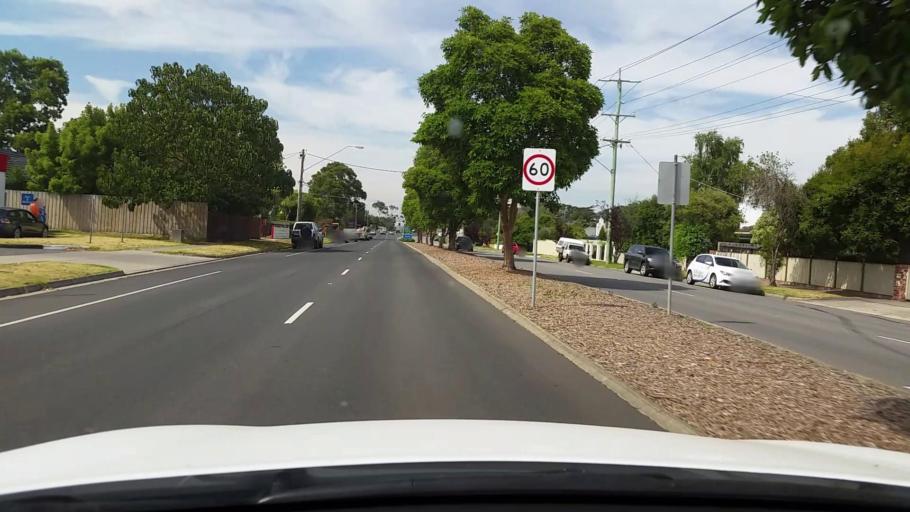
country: AU
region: Victoria
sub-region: Mornington Peninsula
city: Tyabb
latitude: -38.2581
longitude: 145.1898
